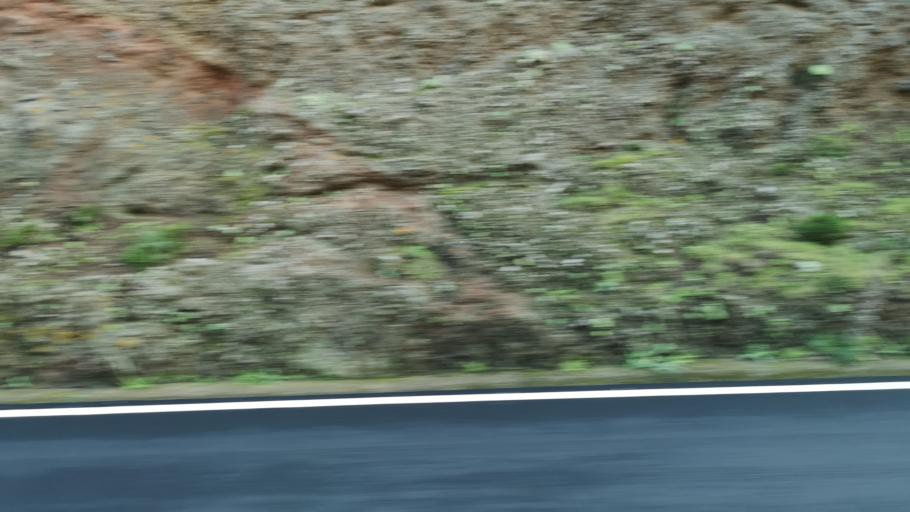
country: ES
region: Canary Islands
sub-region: Provincia de Santa Cruz de Tenerife
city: San Sebastian de la Gomera
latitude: 28.0981
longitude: -17.1760
